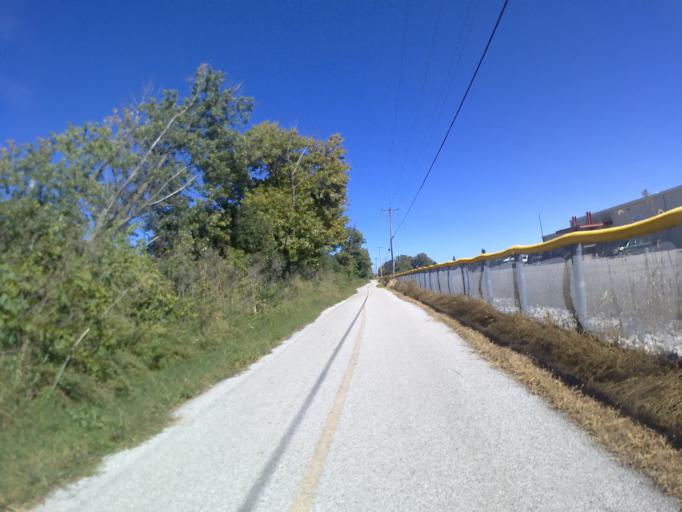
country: US
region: Illinois
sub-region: Cook County
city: Lemont
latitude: 41.6742
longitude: -88.0238
